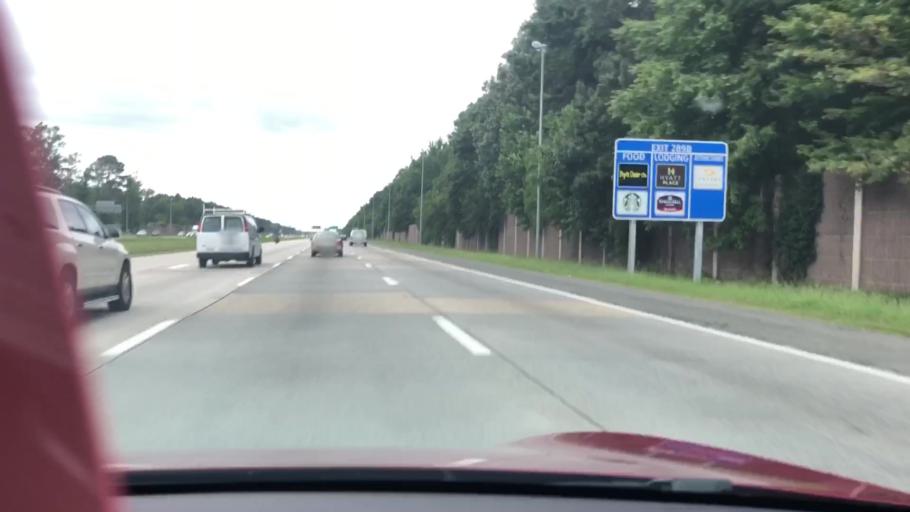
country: US
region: Virginia
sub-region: City of Chesapeake
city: Chesapeake
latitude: 36.7930
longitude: -76.2163
